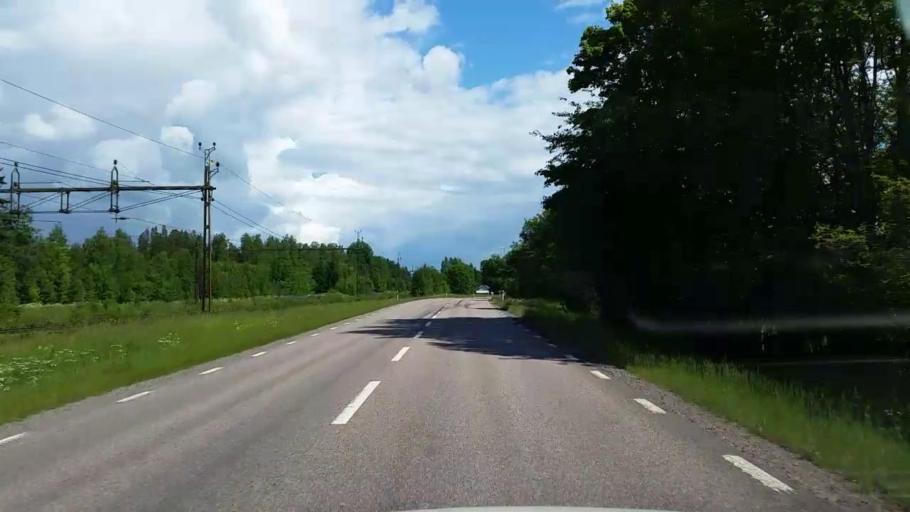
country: SE
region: Dalarna
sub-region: Avesta Kommun
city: Avesta
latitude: 60.1568
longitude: 16.2545
